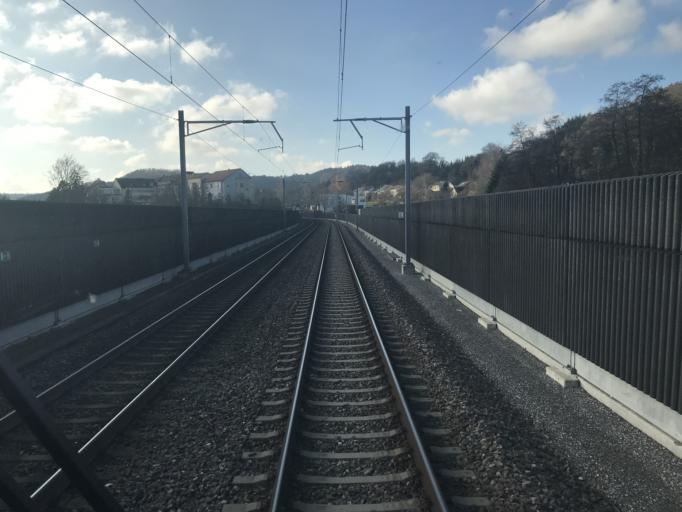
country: DE
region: Baden-Wuerttemberg
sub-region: Freiburg Region
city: Jestetten
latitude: 47.6537
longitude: 8.5697
